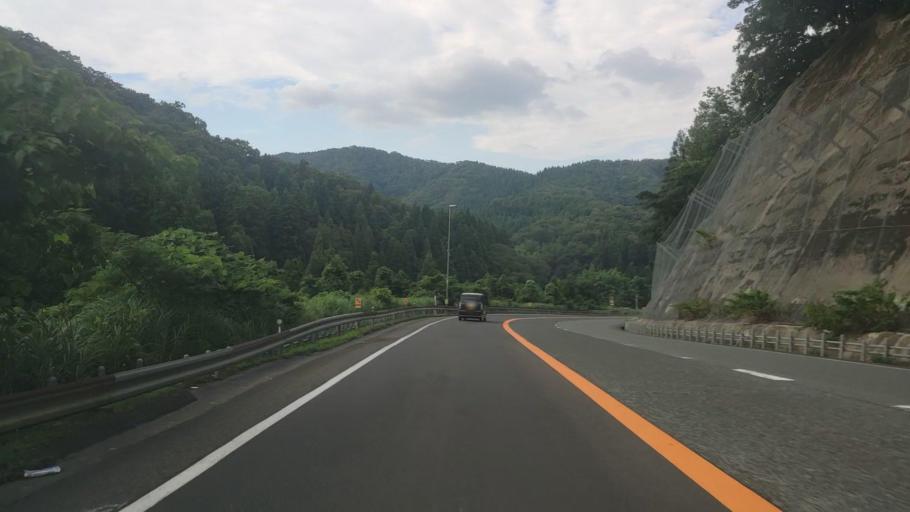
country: JP
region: Fukui
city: Takefu
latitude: 35.8514
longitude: 136.1282
